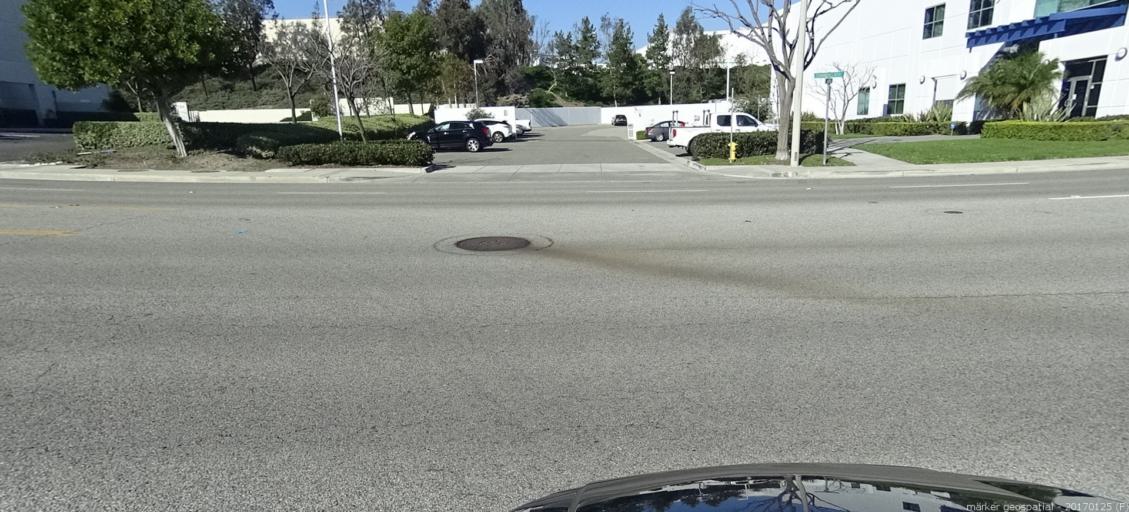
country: US
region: California
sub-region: Orange County
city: Lake Forest
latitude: 33.6643
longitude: -117.6769
